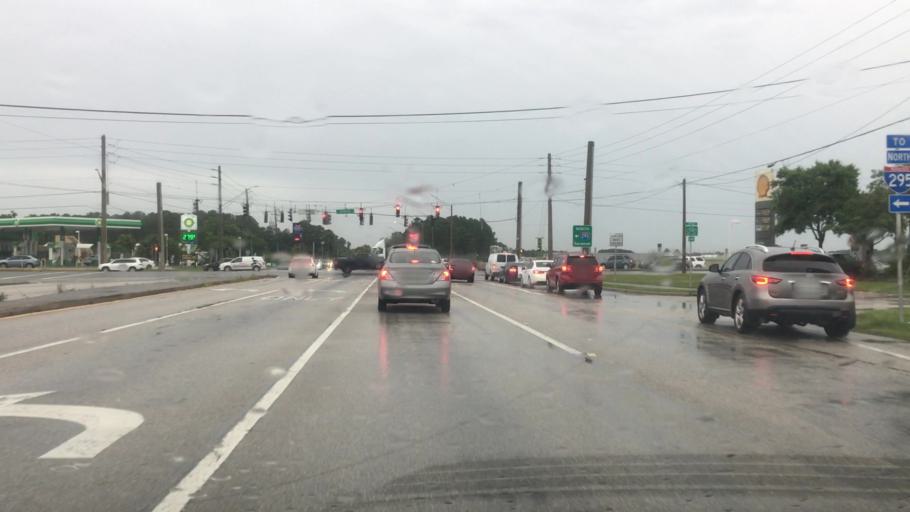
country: US
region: Florida
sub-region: Duval County
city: Atlantic Beach
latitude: 30.3237
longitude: -81.5230
